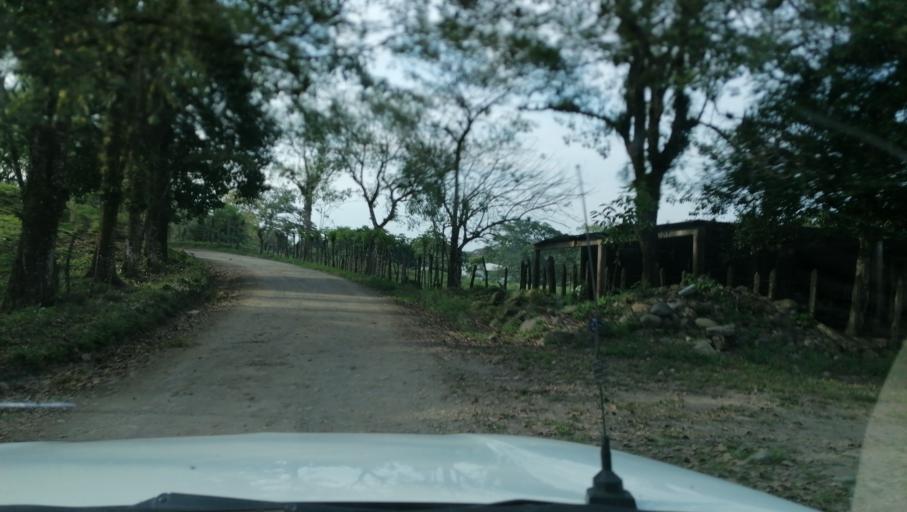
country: MX
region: Chiapas
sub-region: Juarez
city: El Triunfo 1ra. Seccion (Cardona)
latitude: 17.4850
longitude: -93.2416
